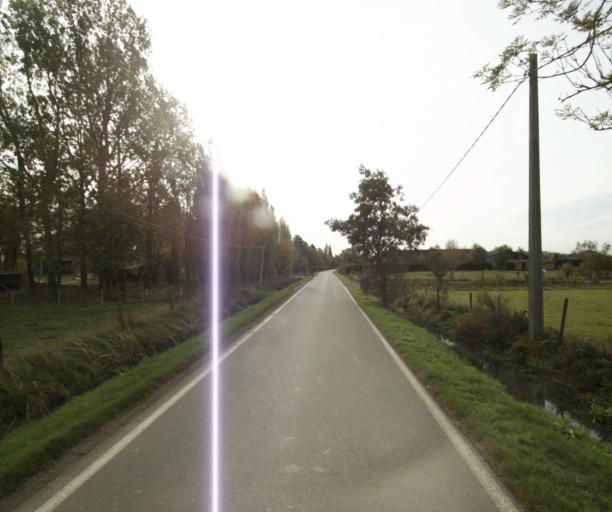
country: FR
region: Nord-Pas-de-Calais
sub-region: Departement du Nord
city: Aubers
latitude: 50.6154
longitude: 2.8454
